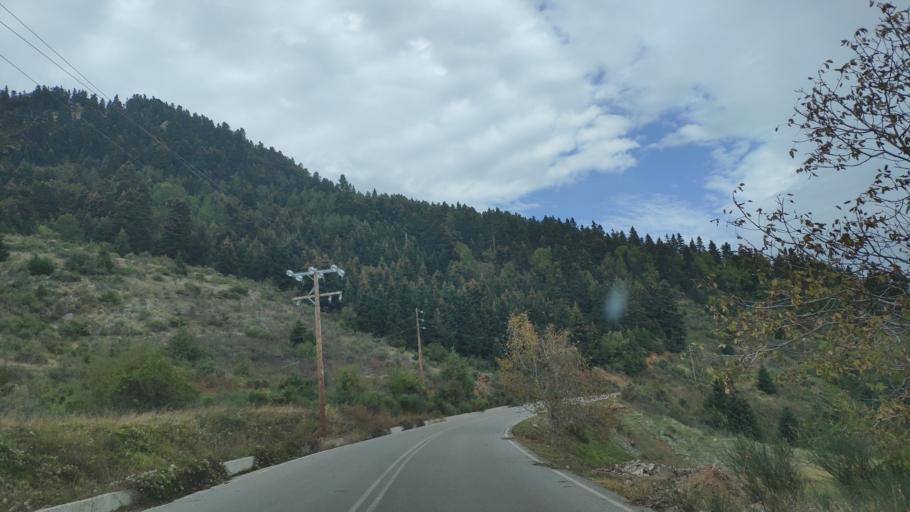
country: GR
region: Central Greece
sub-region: Nomos Fokidos
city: Amfissa
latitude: 38.6865
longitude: 22.3192
